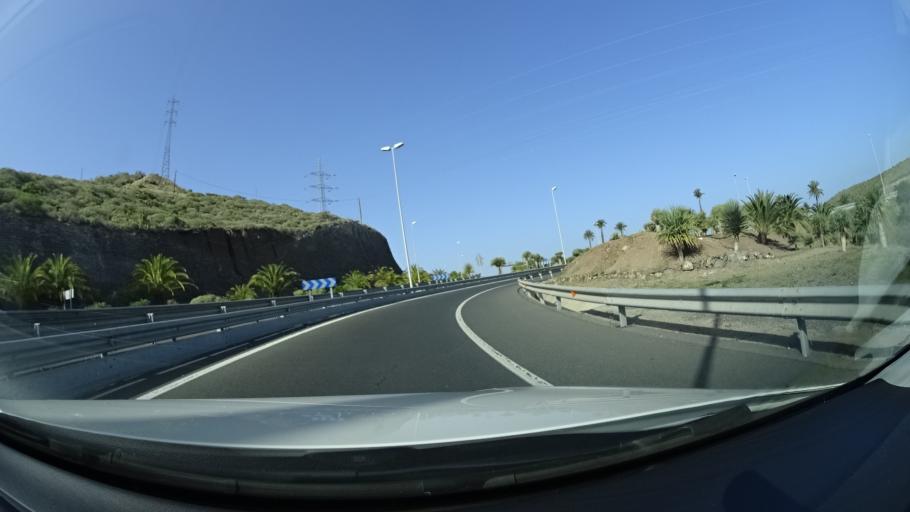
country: ES
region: Canary Islands
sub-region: Provincia de Las Palmas
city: Las Palmas de Gran Canaria
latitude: 28.0745
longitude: -15.4420
